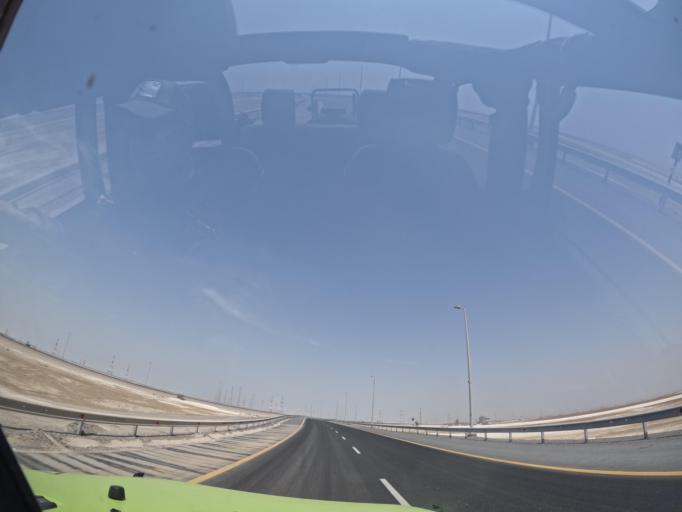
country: AE
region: Abu Dhabi
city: Abu Dhabi
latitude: 24.1472
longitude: 54.2414
